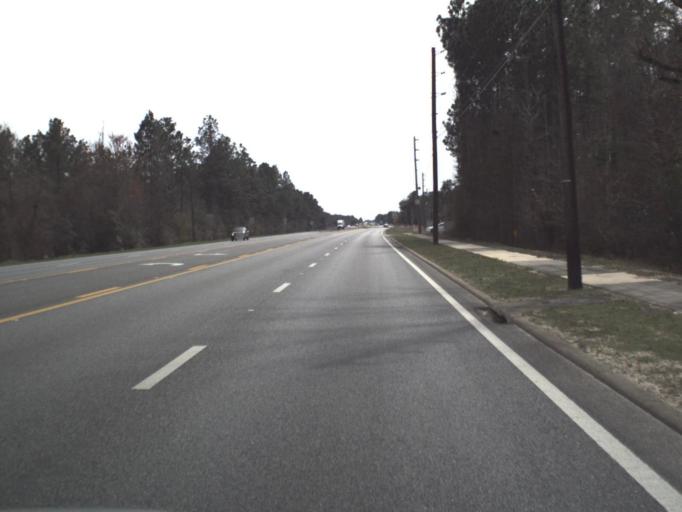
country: US
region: Florida
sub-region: Bay County
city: Youngstown
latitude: 30.4677
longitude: -85.4225
